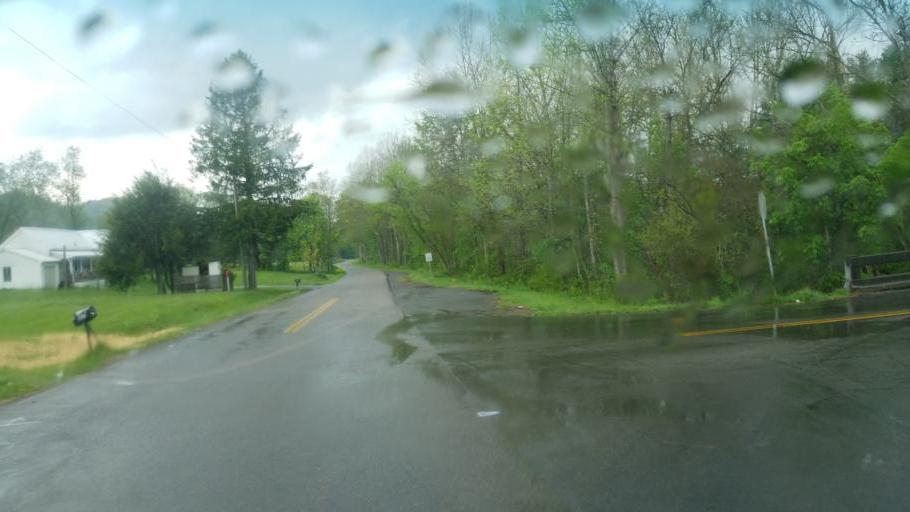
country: US
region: Virginia
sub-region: Smyth County
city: Adwolf
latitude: 36.7683
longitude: -81.5666
